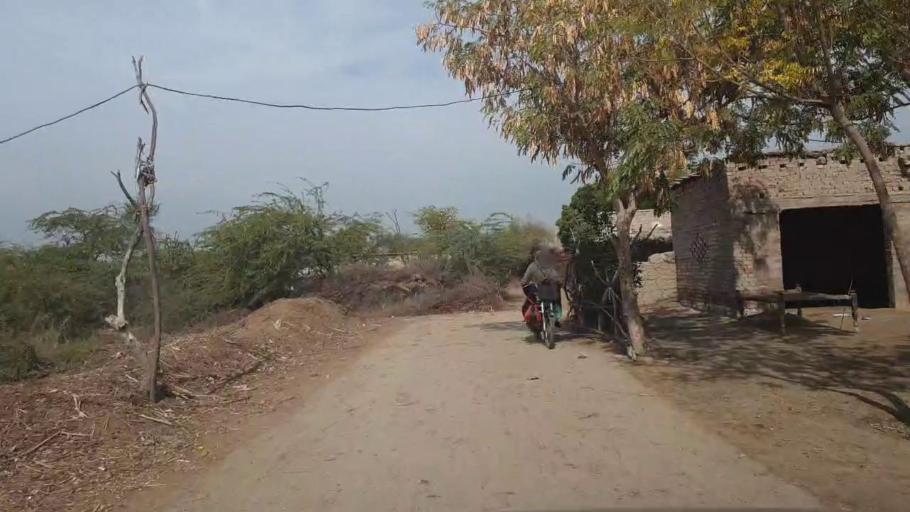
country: PK
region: Sindh
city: Nawabshah
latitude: 26.1262
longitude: 68.4980
